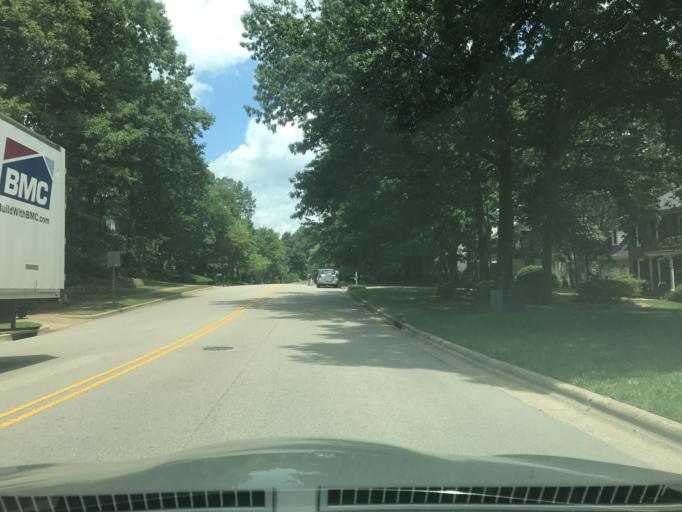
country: US
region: North Carolina
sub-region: Wake County
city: West Raleigh
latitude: 35.8908
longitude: -78.6052
